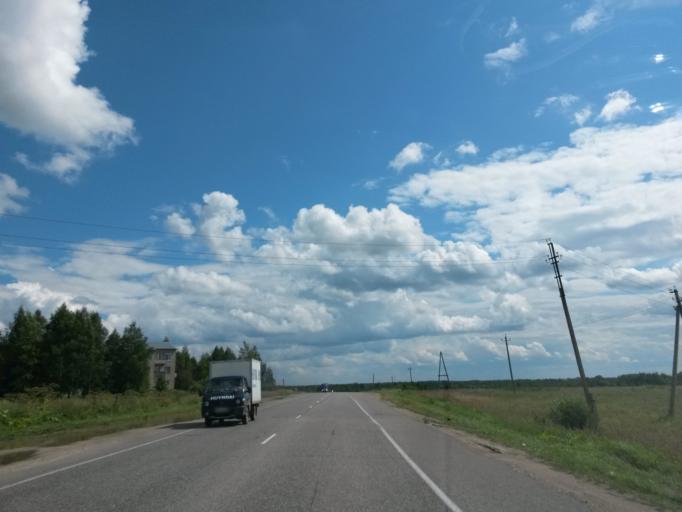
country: RU
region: Ivanovo
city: Pistsovo
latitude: 57.1724
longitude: 40.5094
